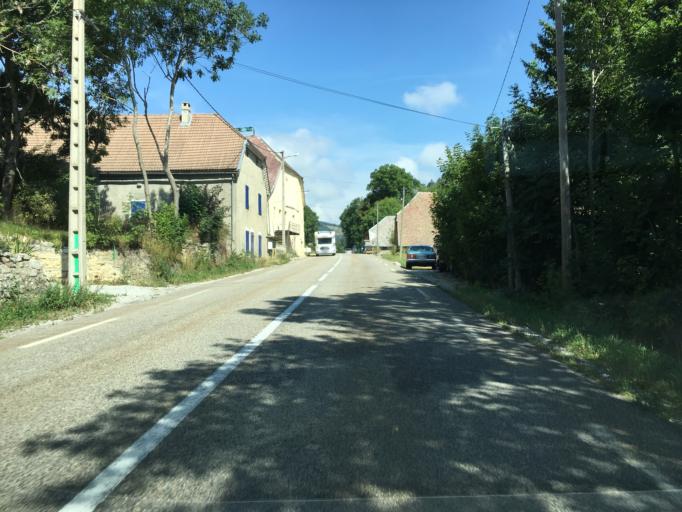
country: FR
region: Rhone-Alpes
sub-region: Departement de l'Isere
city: Mens
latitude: 44.7003
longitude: 5.6821
